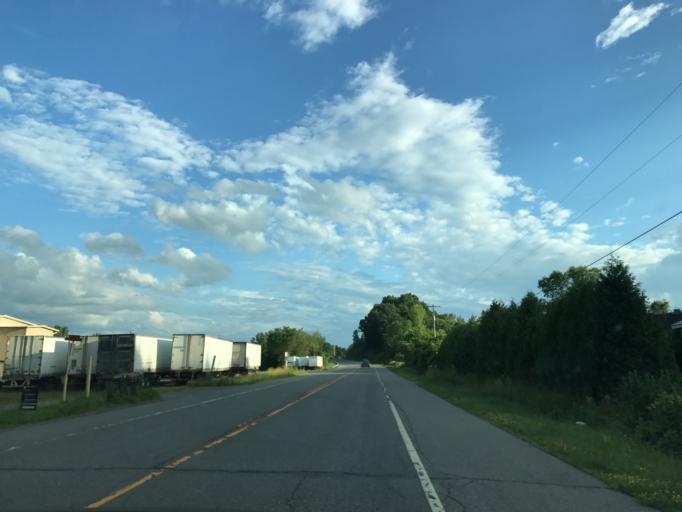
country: US
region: New York
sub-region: Saratoga County
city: Schuylerville
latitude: 43.0728
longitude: -73.5850
